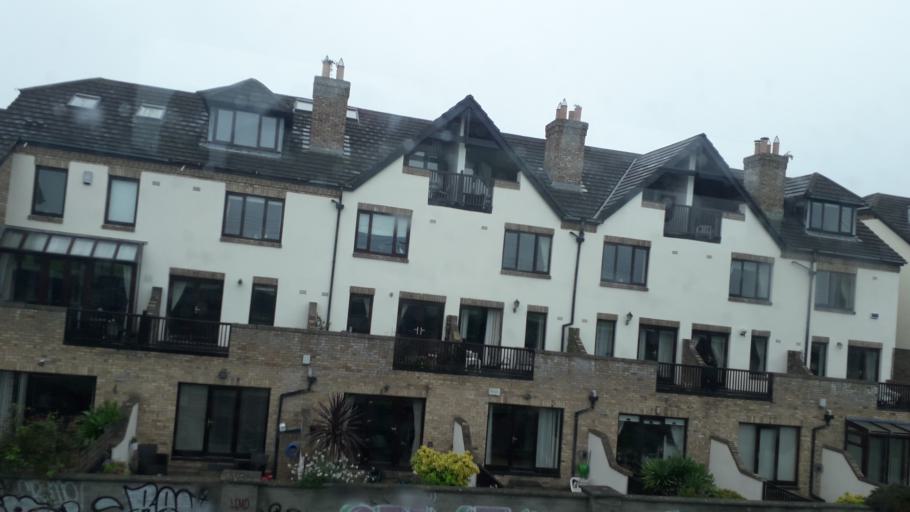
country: IE
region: Leinster
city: Malahide
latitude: 53.4534
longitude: -6.1561
